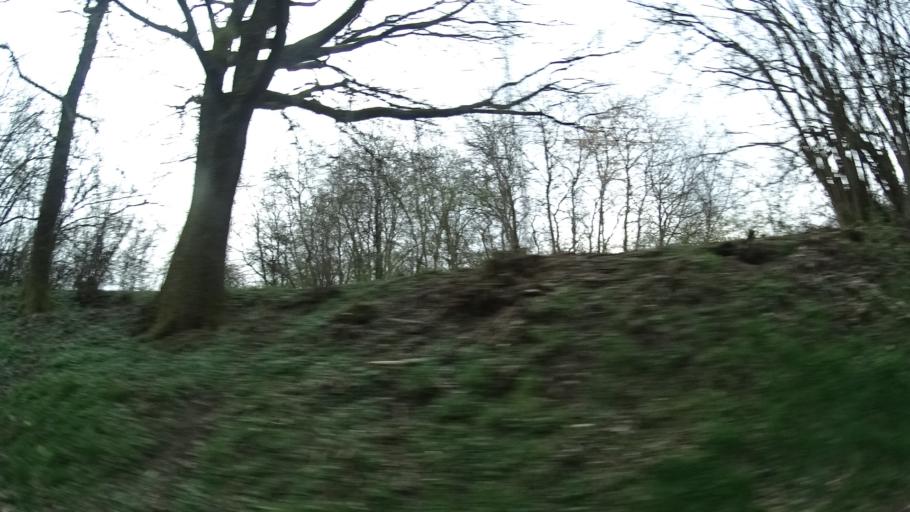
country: DE
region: Rheinland-Pfalz
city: Schmissberg
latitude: 49.6700
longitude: 7.2040
